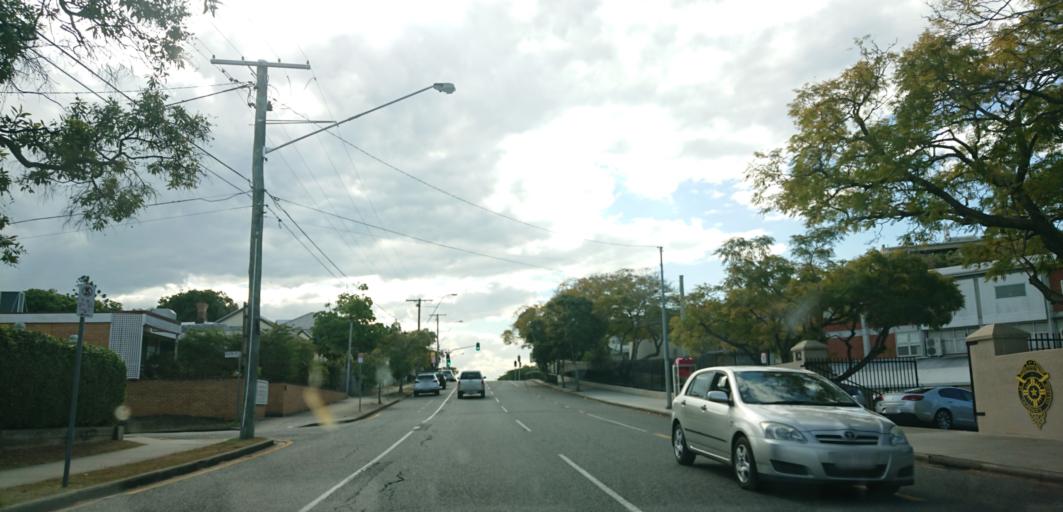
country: AU
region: Queensland
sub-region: Brisbane
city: South Brisbane
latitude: -27.4872
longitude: 153.0249
